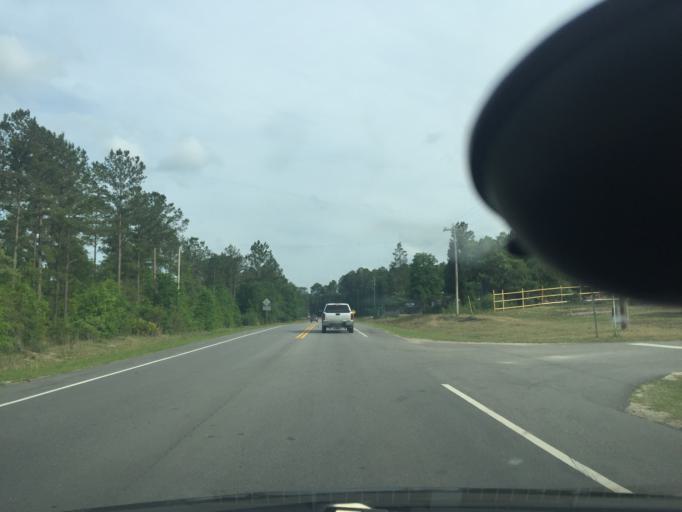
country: US
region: Georgia
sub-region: Chatham County
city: Bloomingdale
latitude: 32.0794
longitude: -81.3702
